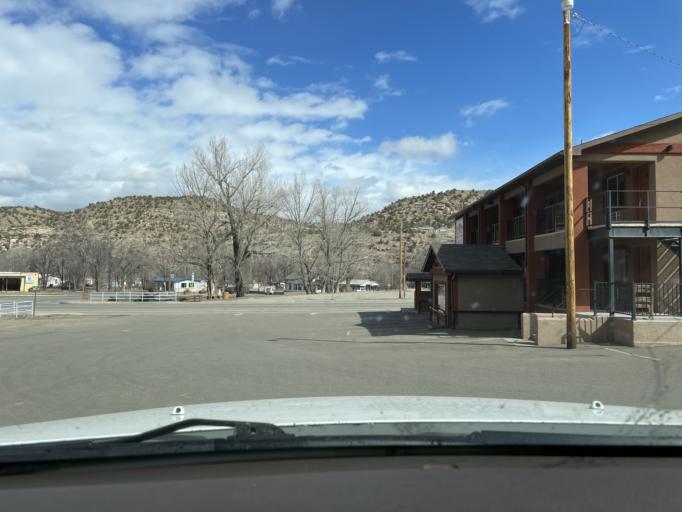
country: US
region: Colorado
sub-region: Dolores County
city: Dove Creek
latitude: 38.2164
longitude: -108.5674
